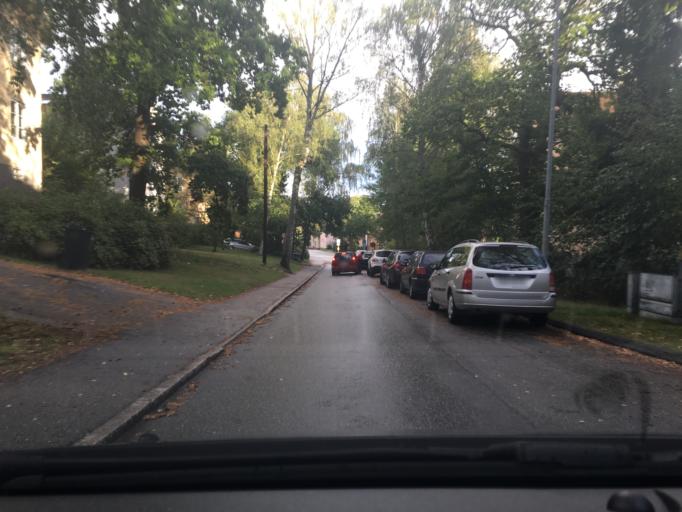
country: SE
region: Stockholm
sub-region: Stockholms Kommun
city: Bromma
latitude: 59.3296
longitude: 17.9659
